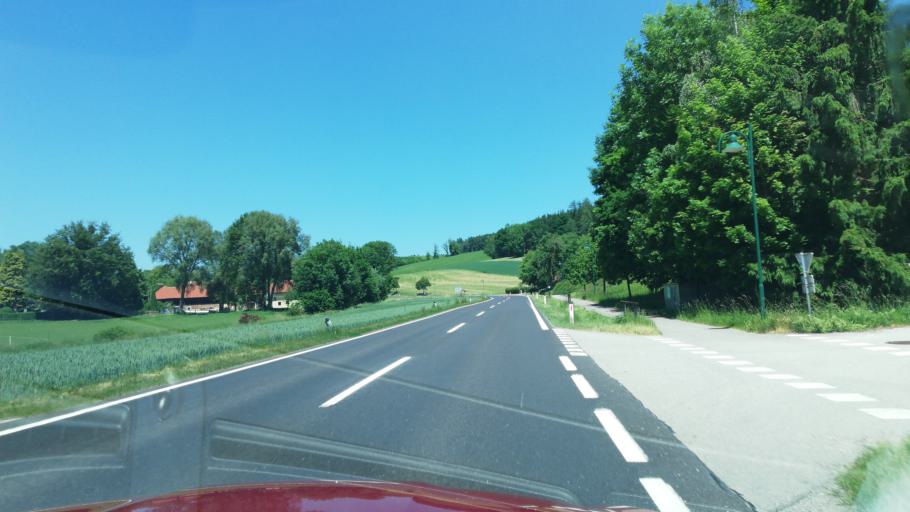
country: AT
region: Upper Austria
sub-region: Politischer Bezirk Vocklabruck
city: Oberndorf bei Schwanenstadt
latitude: 48.0709
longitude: 13.7649
